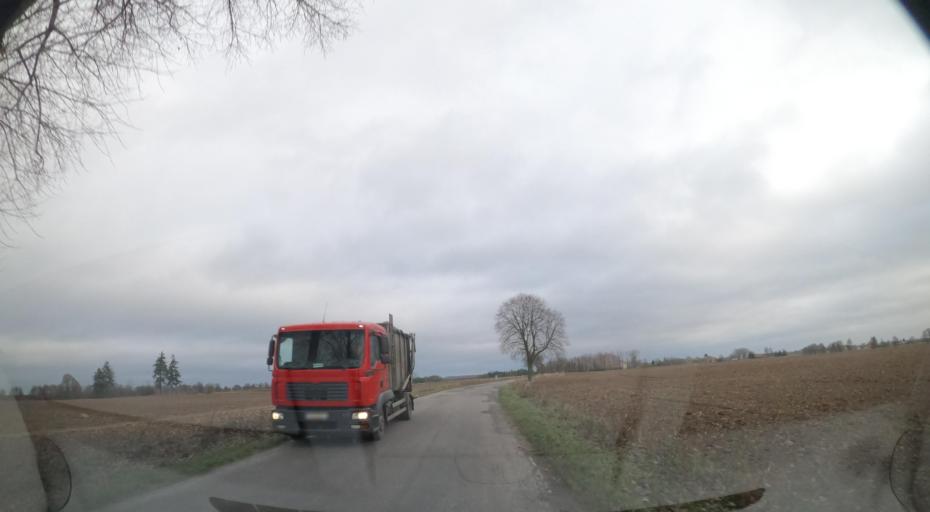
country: PL
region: Greater Poland Voivodeship
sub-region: Powiat pilski
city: Lobzenica
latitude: 53.2661
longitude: 17.1905
